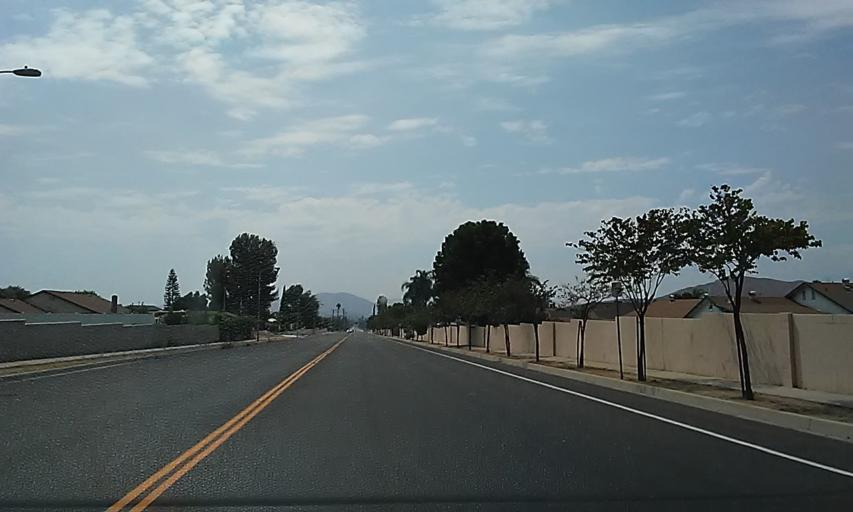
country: US
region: California
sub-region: San Bernardino County
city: Grand Terrace
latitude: 34.0193
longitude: -117.3156
